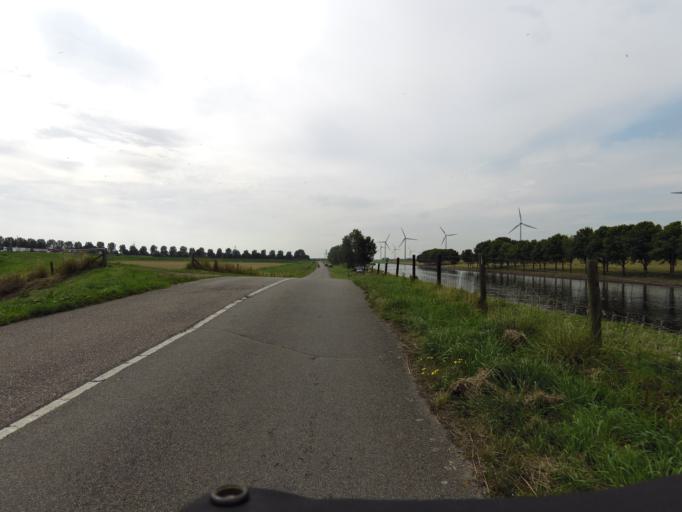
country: NL
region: South Holland
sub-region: Gemeente Spijkenisse
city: Spijkenisse
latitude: 51.8629
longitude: 4.2953
